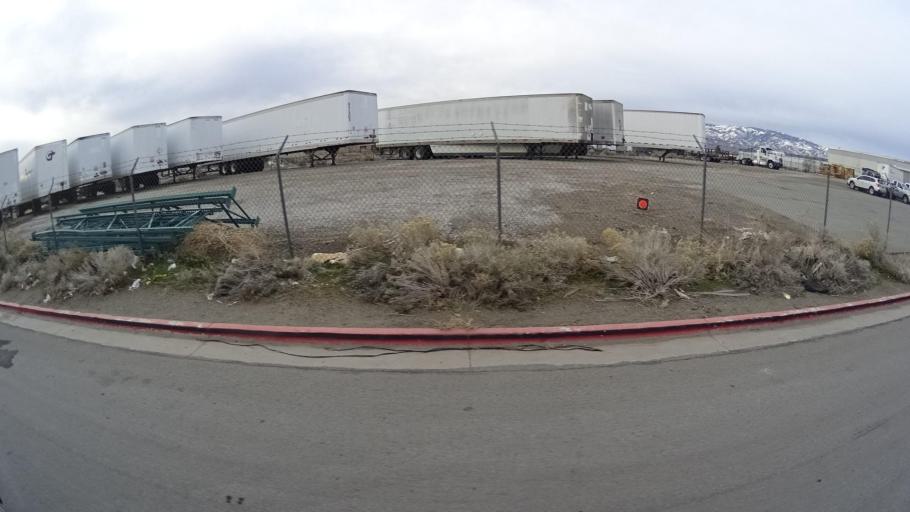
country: US
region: Nevada
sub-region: Washoe County
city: Reno
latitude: 39.5722
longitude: -119.8152
